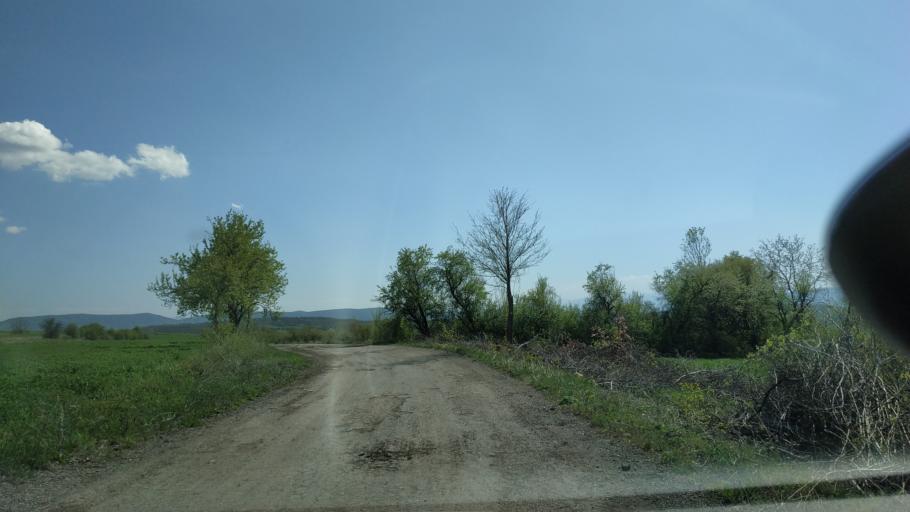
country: RS
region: Central Serbia
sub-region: Zajecarski Okrug
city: Soko Banja
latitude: 43.5278
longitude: 21.9061
